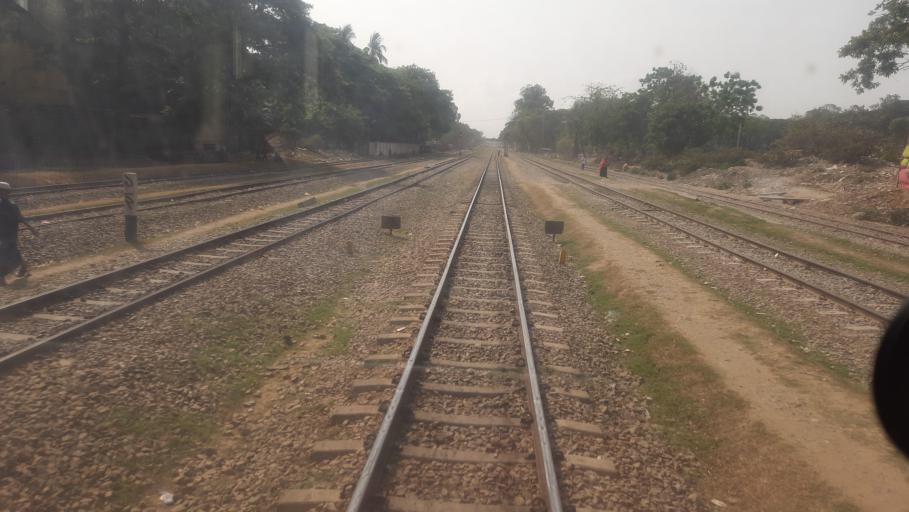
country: BD
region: Chittagong
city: Chittagong
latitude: 22.3376
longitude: 91.8189
